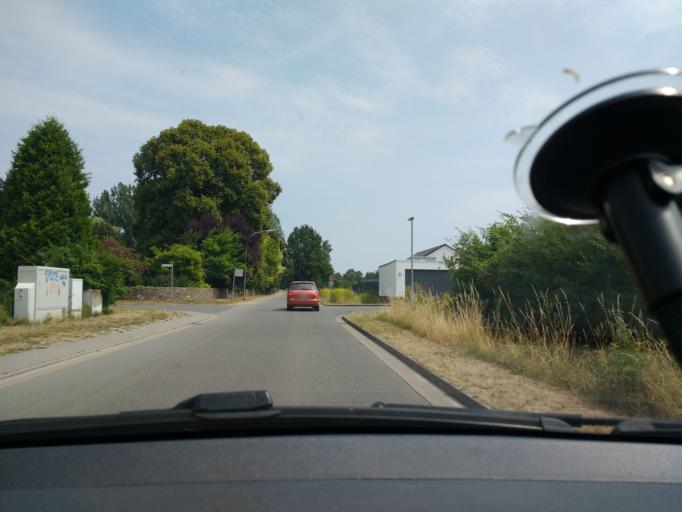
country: DE
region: Lower Saxony
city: Wagenhoff
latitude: 52.5147
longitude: 10.5467
